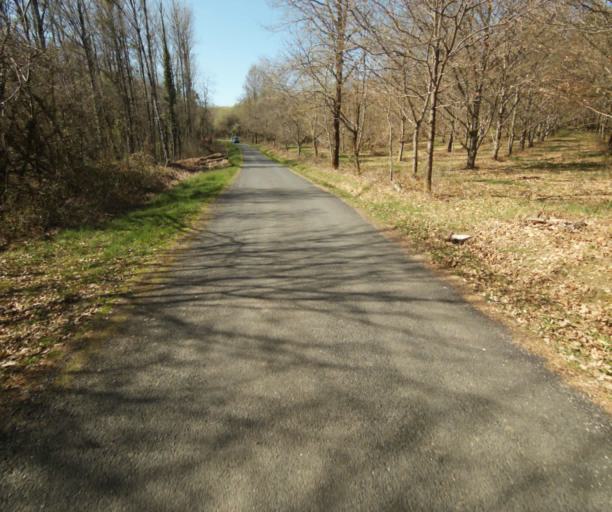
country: FR
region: Limousin
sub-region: Departement de la Correze
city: Chameyrat
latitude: 45.2888
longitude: 1.7069
